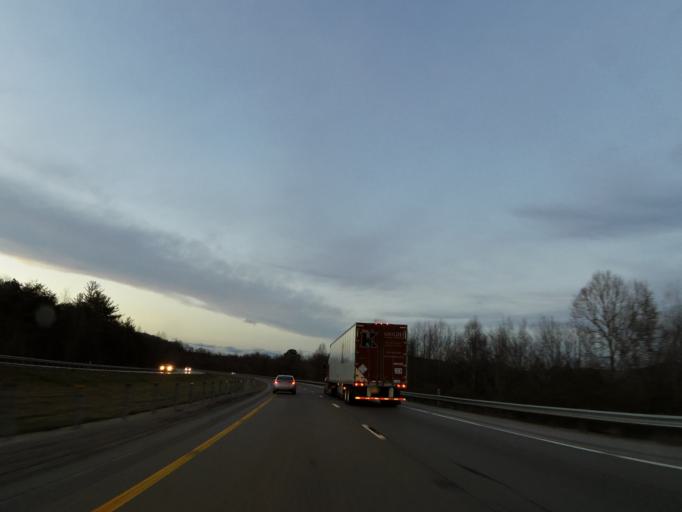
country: US
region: Tennessee
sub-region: Campbell County
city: Jellico
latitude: 36.6220
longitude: -84.1070
